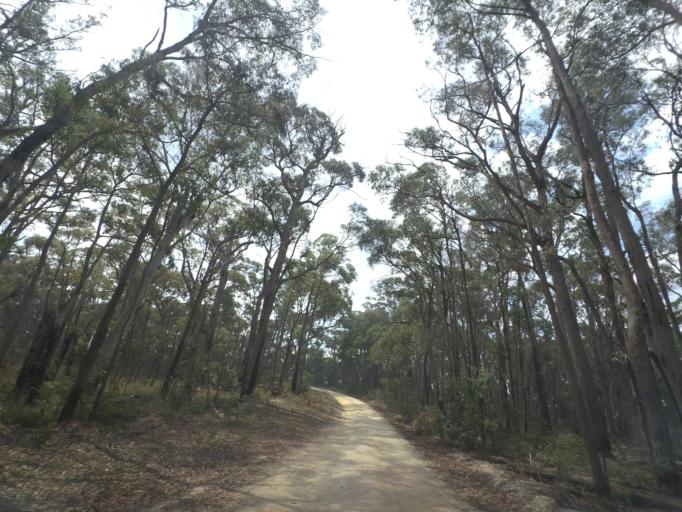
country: AU
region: Victoria
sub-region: Moorabool
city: Bacchus Marsh
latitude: -37.5062
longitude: 144.4285
